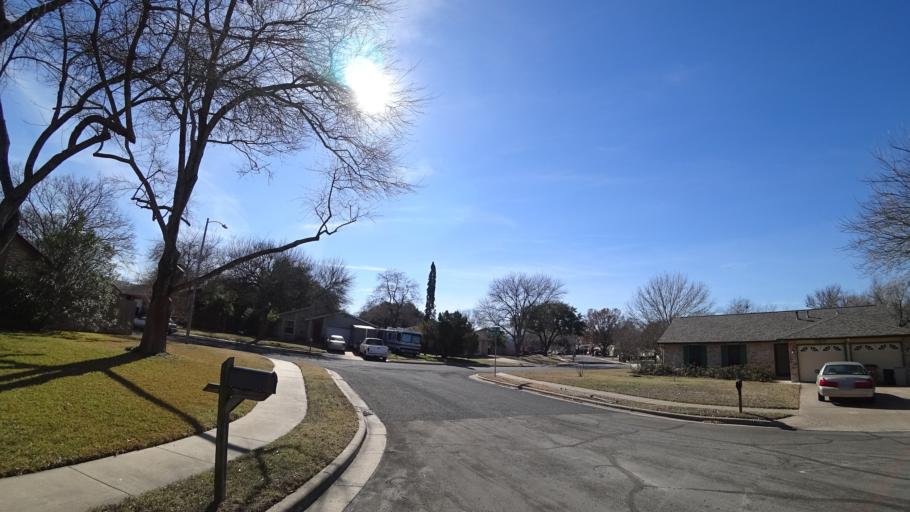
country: US
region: Texas
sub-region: Travis County
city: Wells Branch
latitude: 30.3871
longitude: -97.6997
